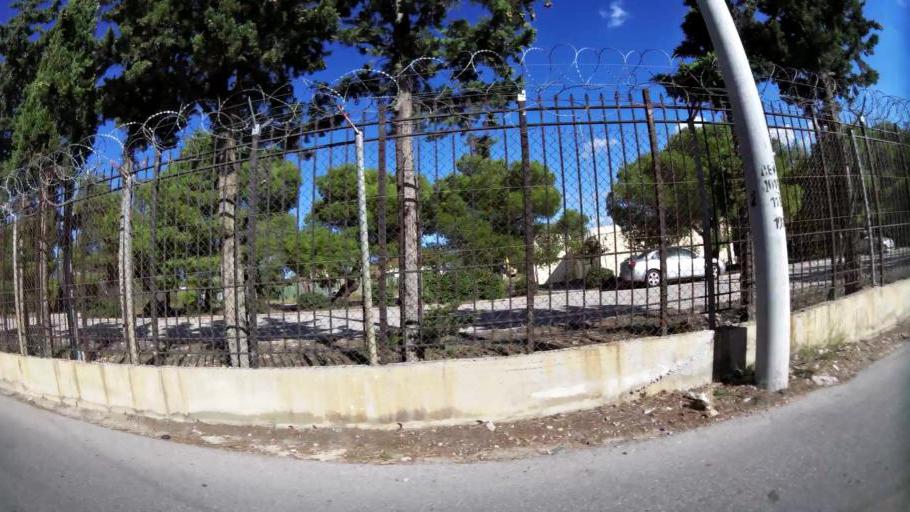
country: GR
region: Attica
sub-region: Nomarchia Anatolikis Attikis
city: Acharnes
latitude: 38.1043
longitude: 23.7235
